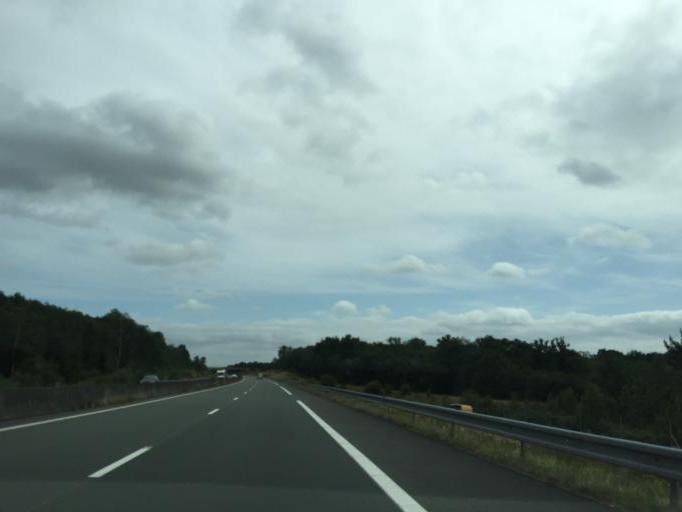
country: FR
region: Pays de la Loire
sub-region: Departement de la Sarthe
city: Mayet
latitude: 47.7372
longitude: 0.3232
